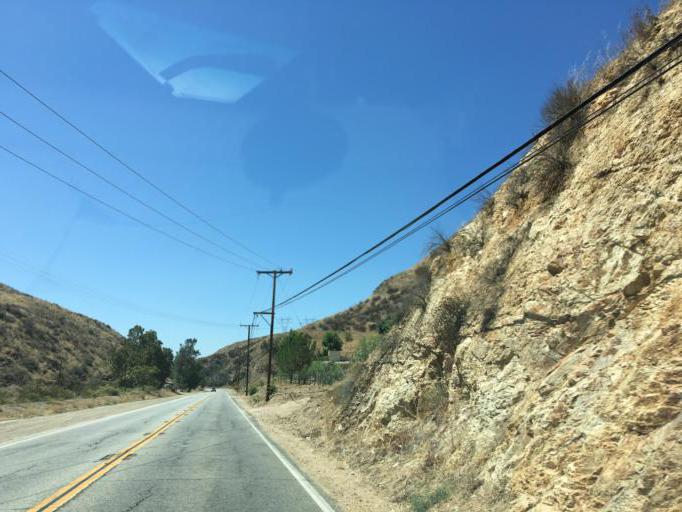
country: US
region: California
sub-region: Los Angeles County
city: Agua Dulce
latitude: 34.4947
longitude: -118.3855
